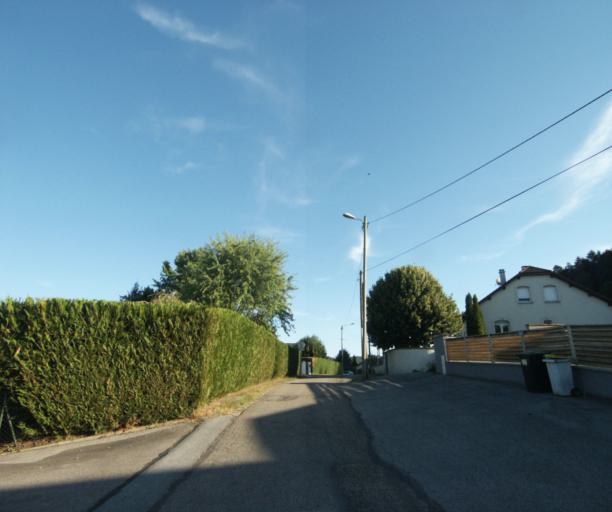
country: FR
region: Lorraine
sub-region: Departement des Vosges
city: Chantraine
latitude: 48.1443
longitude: 6.4495
